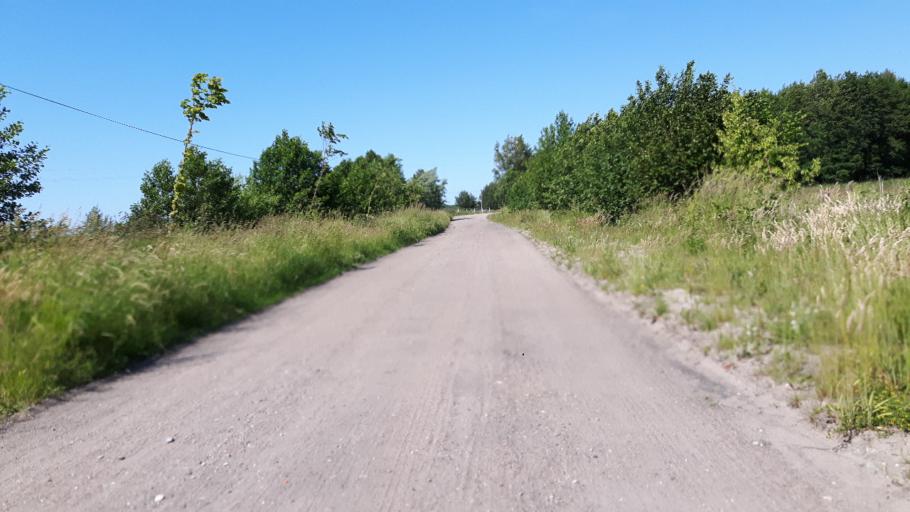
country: PL
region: Pomeranian Voivodeship
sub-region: Powiat slupski
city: Glowczyce
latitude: 54.6806
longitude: 17.4370
